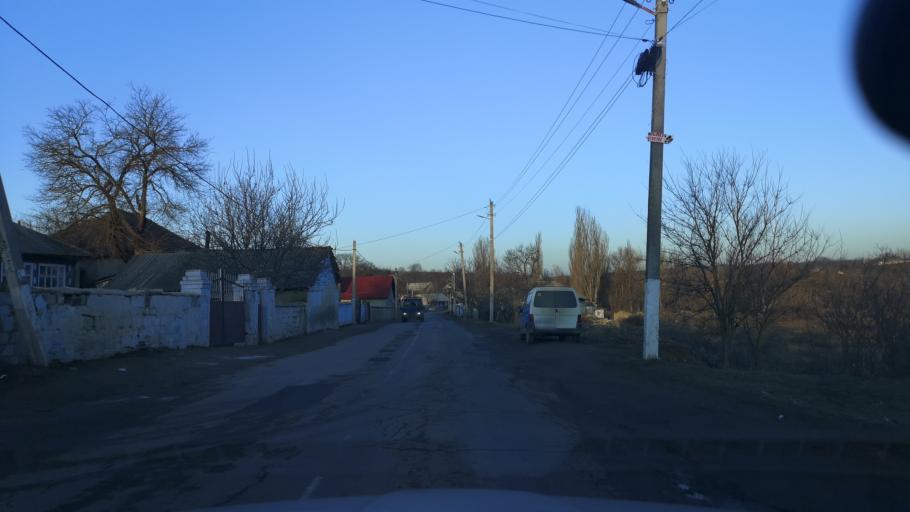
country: MD
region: Orhei
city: Orhei
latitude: 47.3041
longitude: 28.9229
